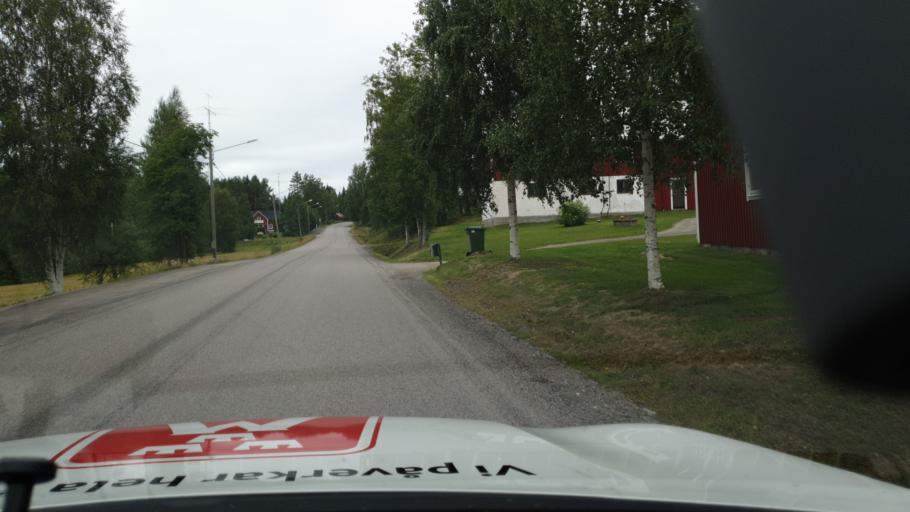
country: SE
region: Vaesterbotten
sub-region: Umea Kommun
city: Ersmark
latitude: 63.9339
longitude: 20.3006
